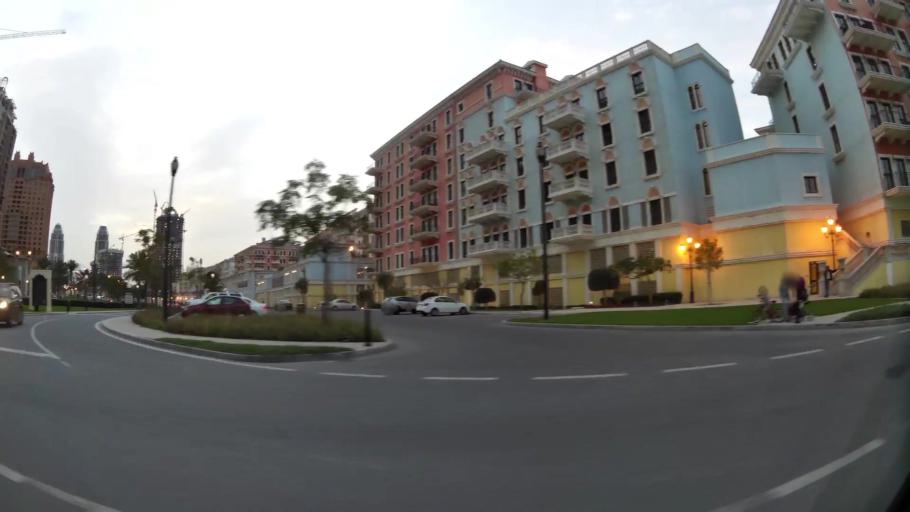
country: QA
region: Baladiyat ad Dawhah
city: Doha
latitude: 25.3752
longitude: 51.5456
